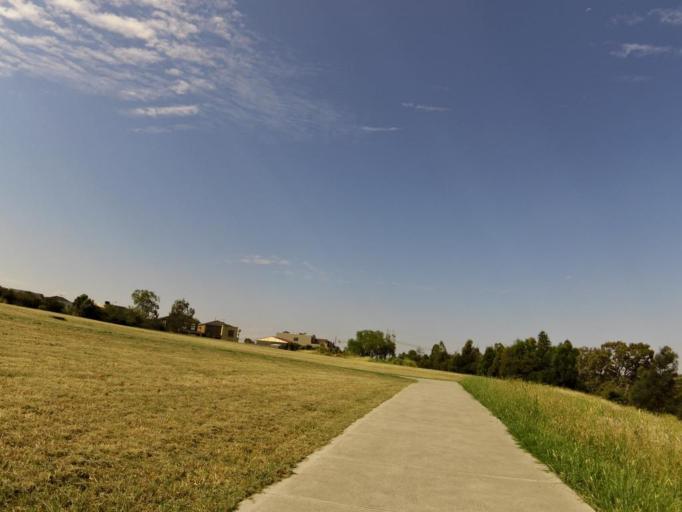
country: AU
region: Victoria
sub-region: Whittlesea
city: Epping
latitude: -37.6347
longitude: 145.0353
